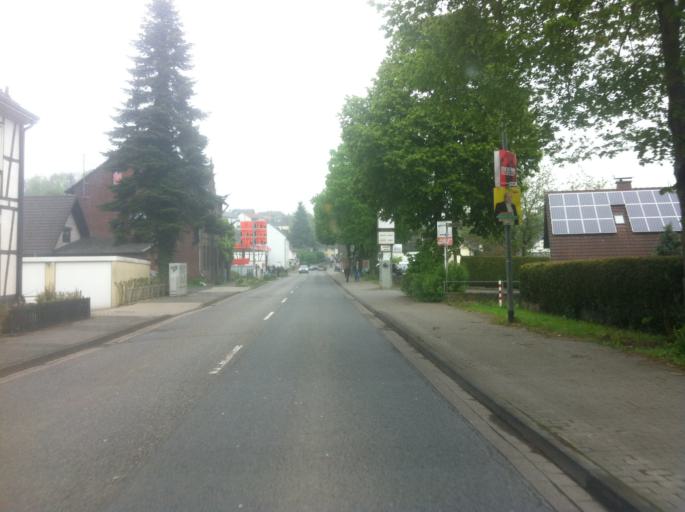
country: DE
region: North Rhine-Westphalia
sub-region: Regierungsbezirk Koln
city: Hennef
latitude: 50.7900
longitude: 7.3264
